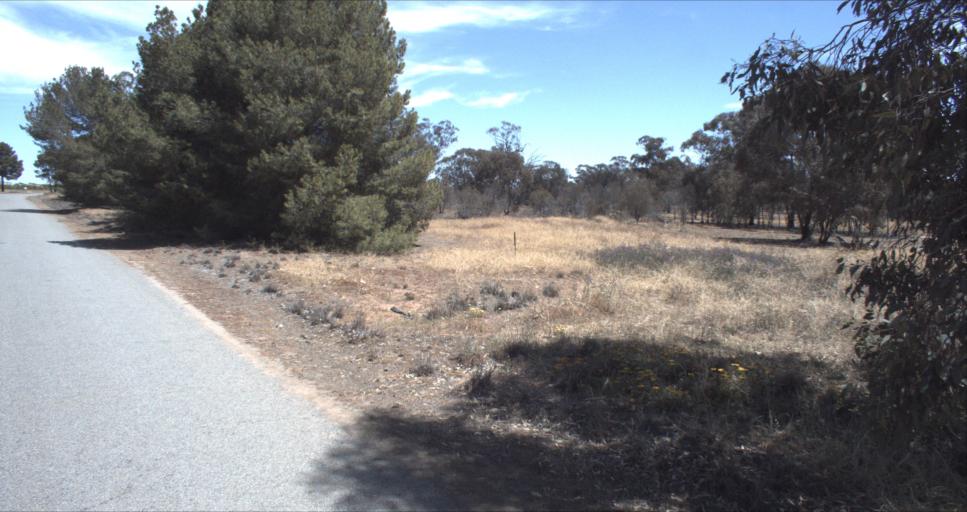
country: AU
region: New South Wales
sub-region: Narrandera
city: Narrandera
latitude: -34.6761
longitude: 146.4421
